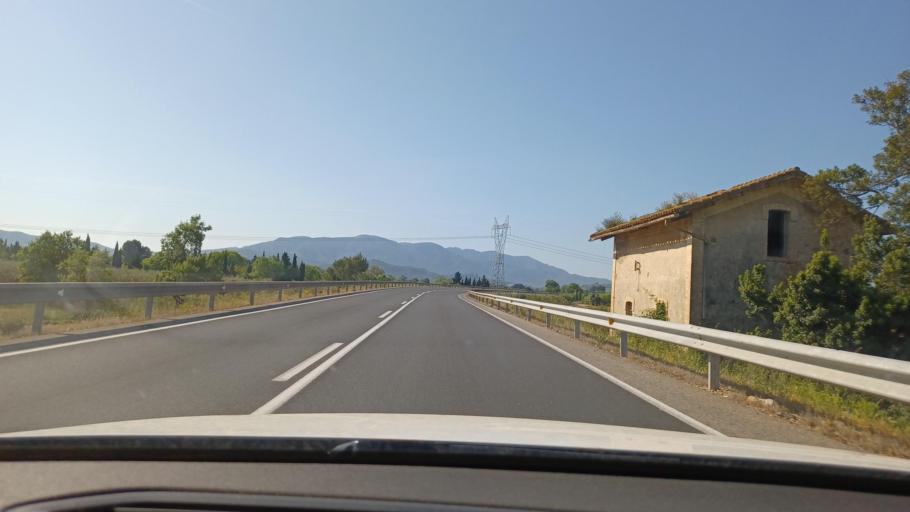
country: ES
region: Catalonia
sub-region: Provincia de Tarragona
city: Santa Barbara
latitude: 40.7128
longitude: 0.5066
